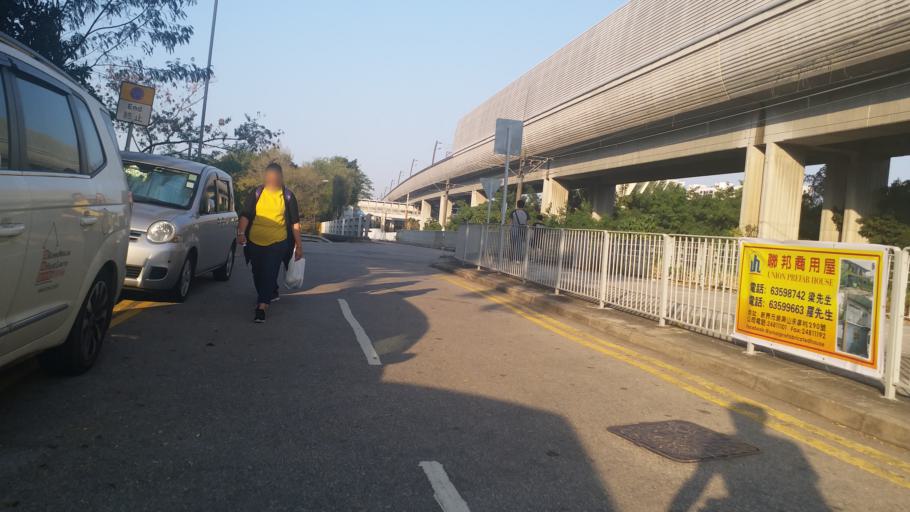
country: HK
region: Tuen Mun
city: Tuen Mun
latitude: 22.4172
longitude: 113.9809
